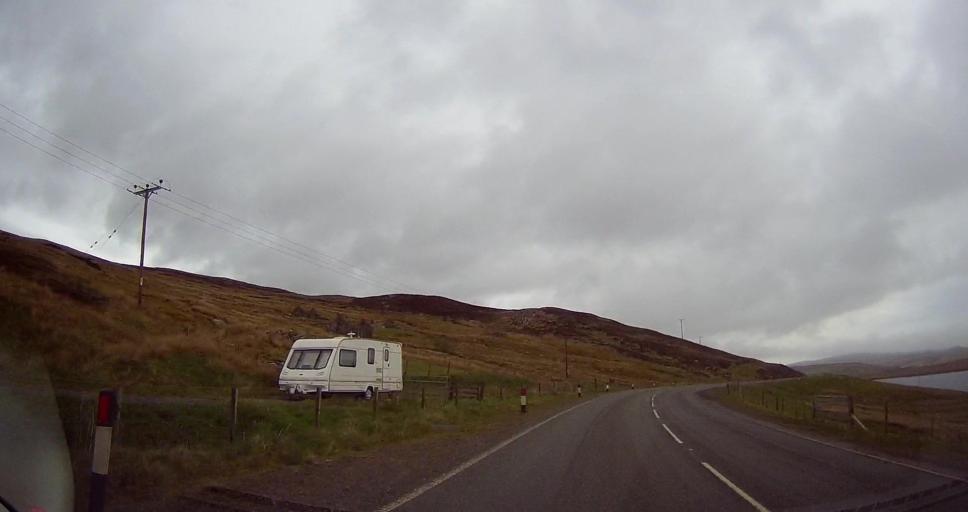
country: GB
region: Scotland
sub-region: Shetland Islands
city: Lerwick
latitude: 60.2552
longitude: -1.2271
